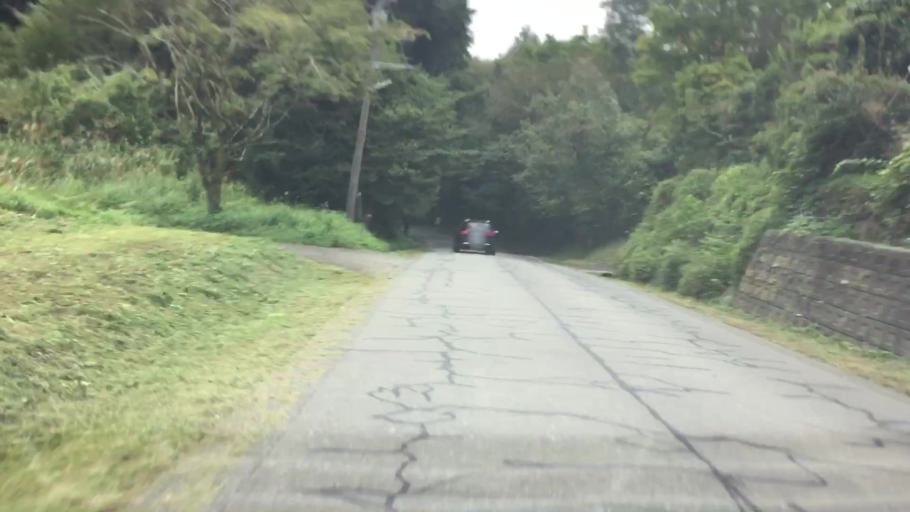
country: JP
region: Shizuoka
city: Fujinomiya
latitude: 35.3598
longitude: 138.5907
